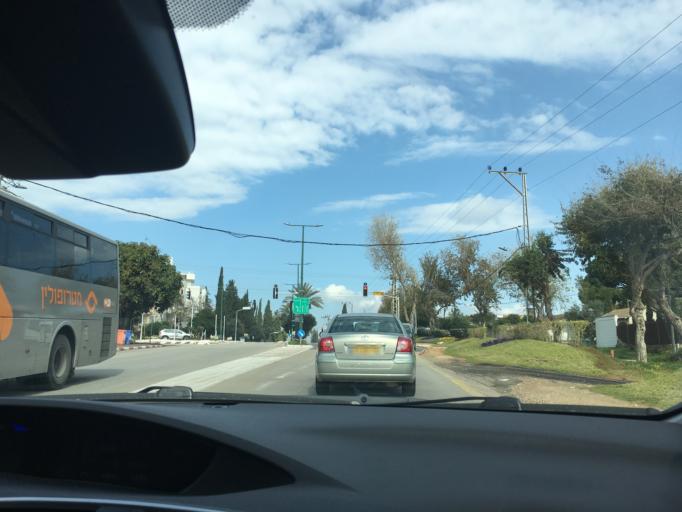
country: IL
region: Tel Aviv
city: Ramat HaSharon
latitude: 32.1671
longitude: 34.8530
